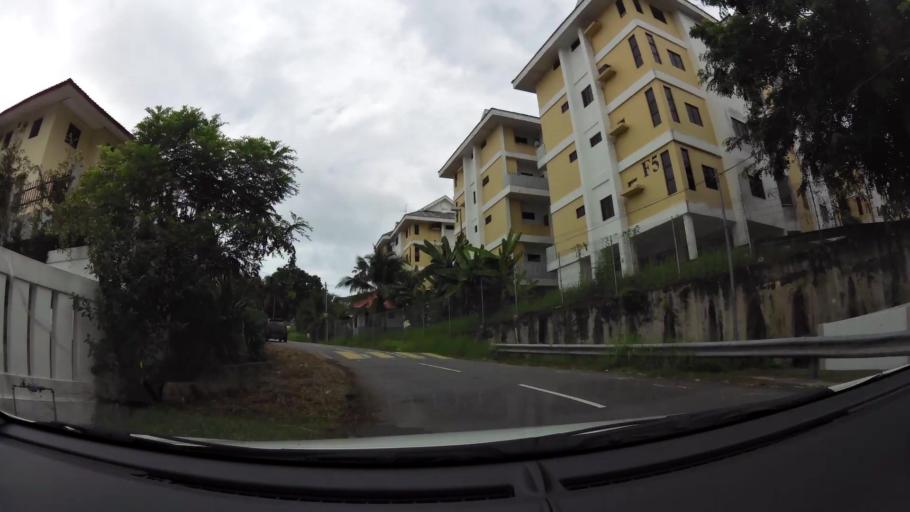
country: BN
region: Brunei and Muara
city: Bandar Seri Begawan
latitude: 4.8919
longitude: 114.9155
